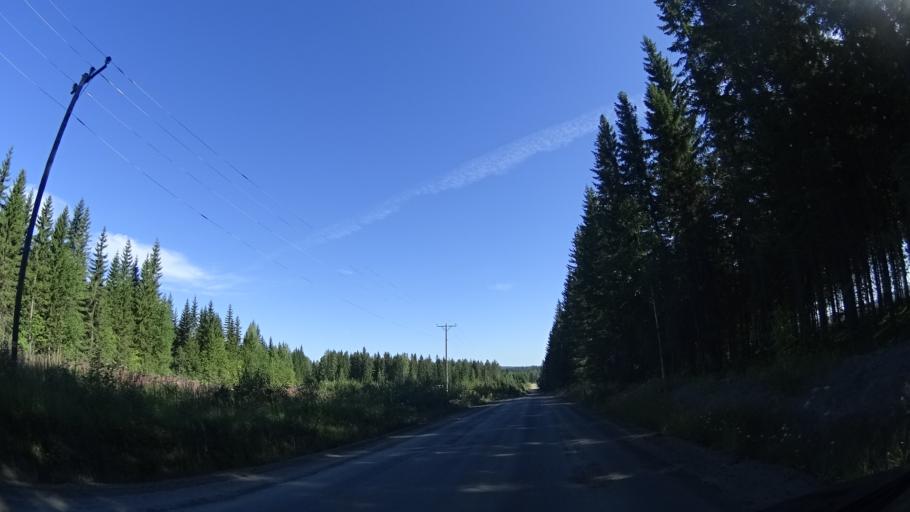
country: FI
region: Central Finland
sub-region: Jyvaeskylae
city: Petaejaevesi
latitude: 62.2960
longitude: 25.3266
